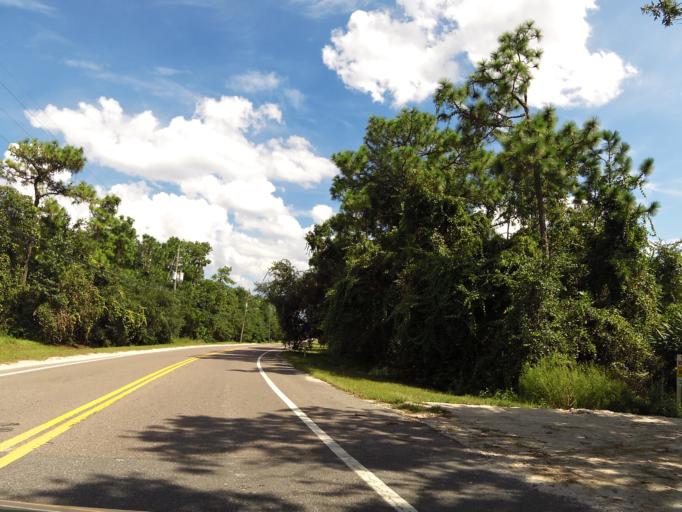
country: US
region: Florida
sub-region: Duval County
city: Jacksonville
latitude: 30.4208
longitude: -81.5703
